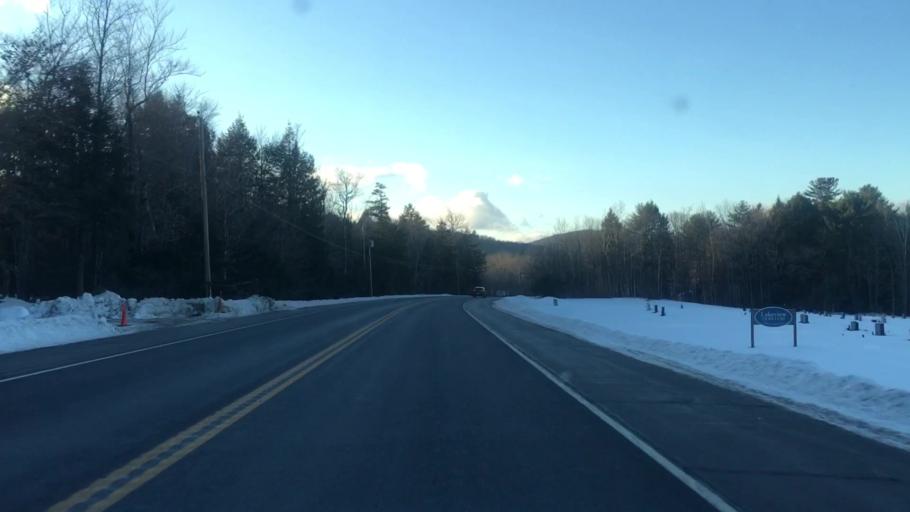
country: US
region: Maine
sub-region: Franklin County
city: Wilton
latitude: 44.5846
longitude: -70.2443
